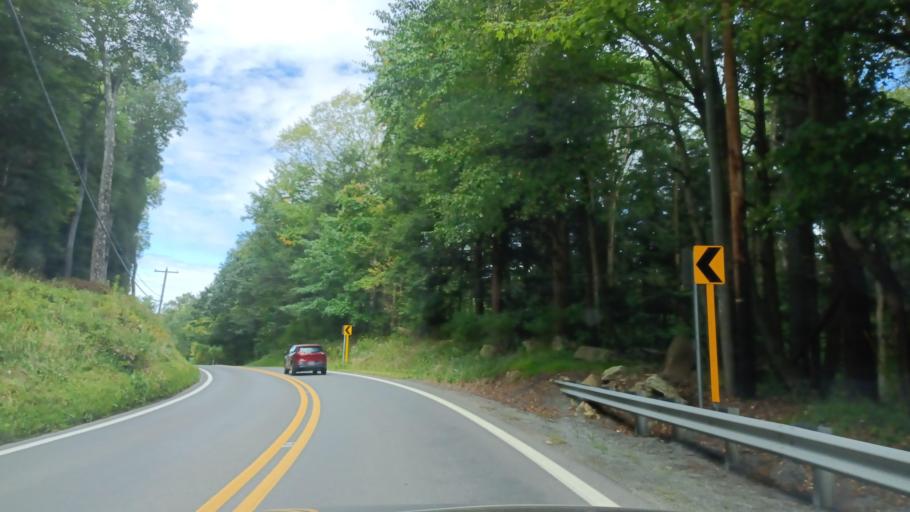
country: US
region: West Virginia
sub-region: Preston County
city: Terra Alta
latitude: 39.3250
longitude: -79.5418
